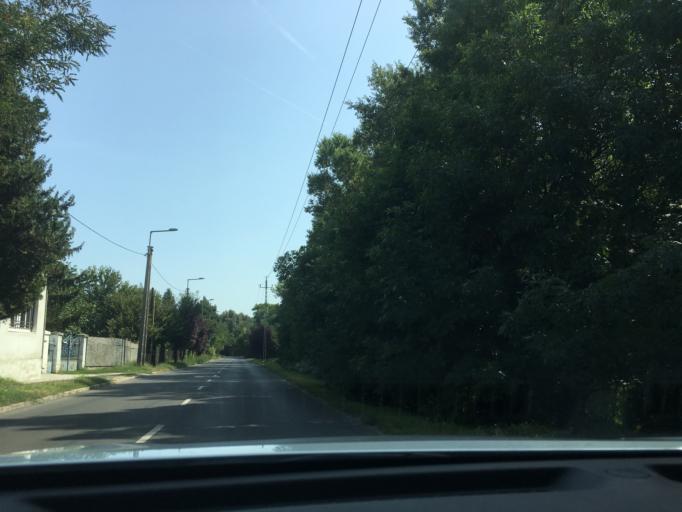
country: HU
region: Budapest
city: Budapest XVII. keruelet
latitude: 47.4861
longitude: 19.2616
